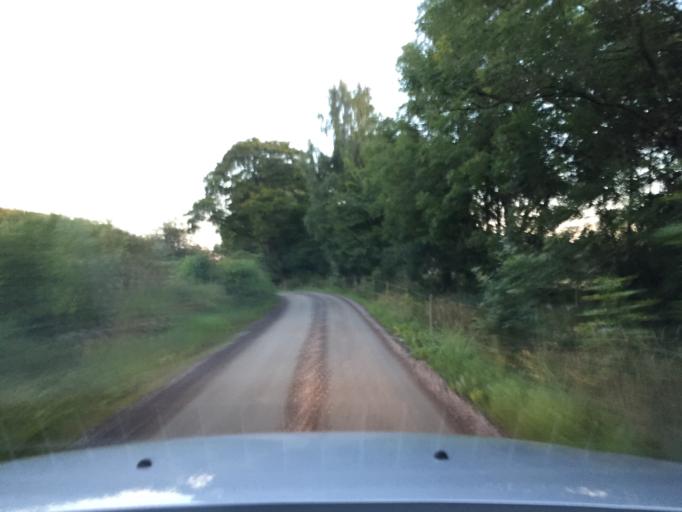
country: SE
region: Skane
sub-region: Hassleholms Kommun
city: Sosdala
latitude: 55.9973
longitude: 13.6674
